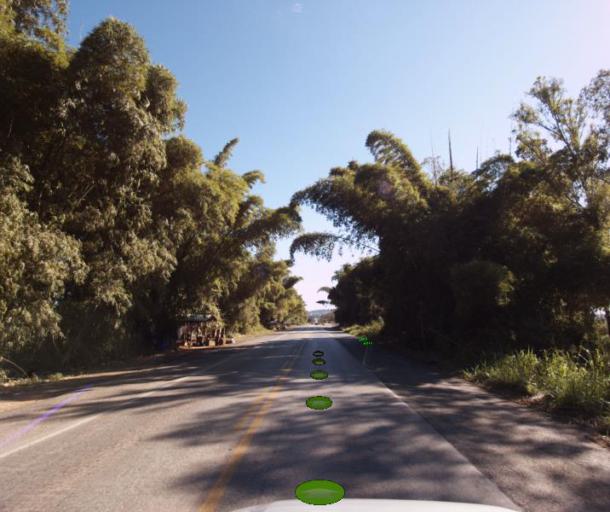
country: BR
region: Goias
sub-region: Uruacu
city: Uruacu
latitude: -14.6251
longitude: -49.1726
